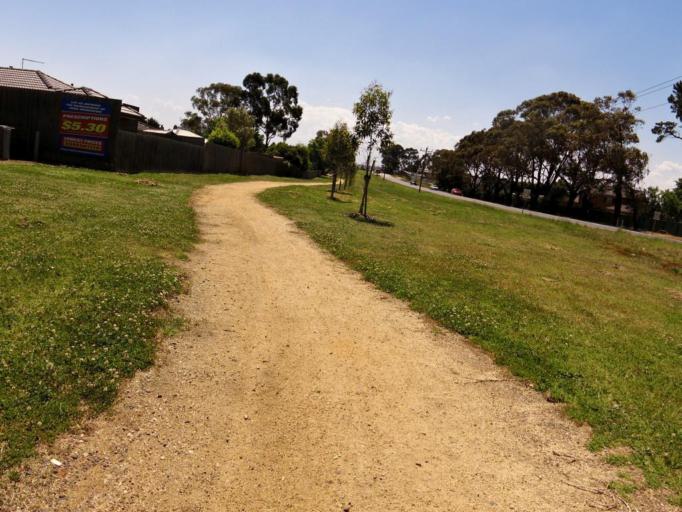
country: AU
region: Victoria
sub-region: Casey
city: Narre Warren South
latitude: -38.0337
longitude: 145.2838
